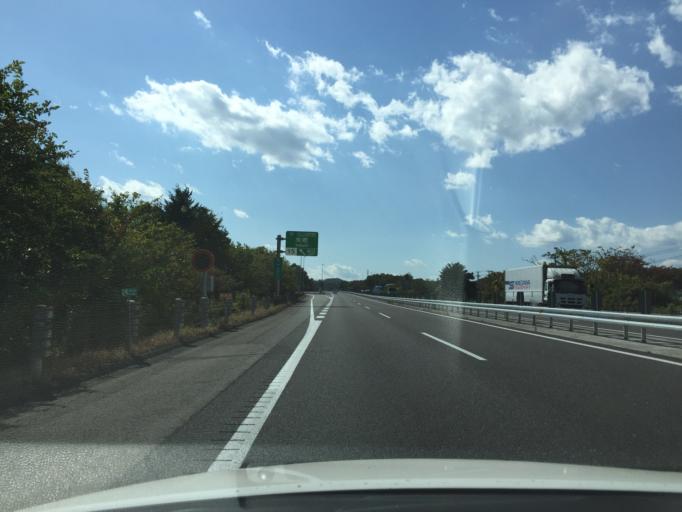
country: JP
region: Fukushima
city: Sukagawa
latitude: 37.1986
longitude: 140.3006
